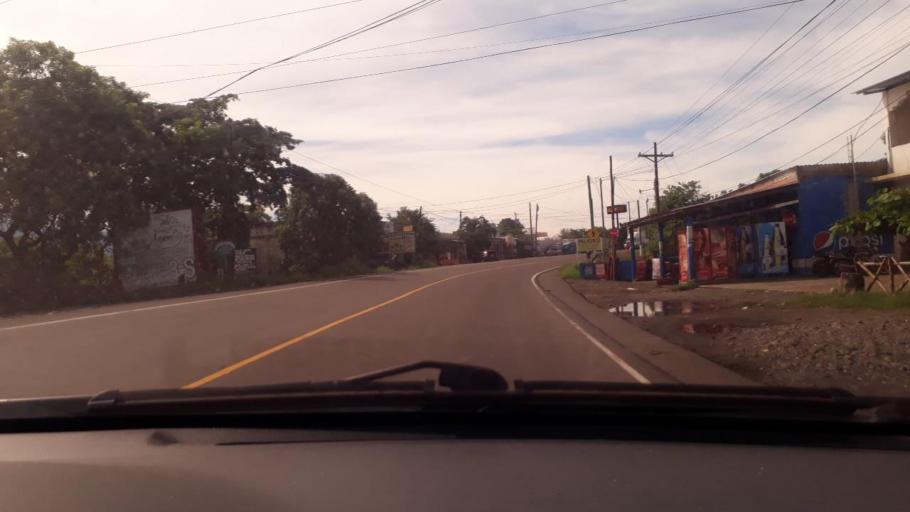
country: SV
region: Ahuachapan
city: San Francisco Menendez
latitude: 13.8805
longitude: -90.0984
